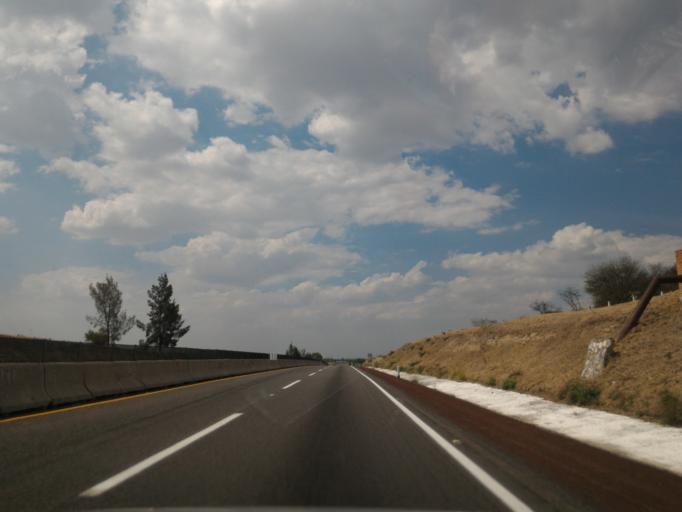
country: MX
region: Jalisco
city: Encarnacion de Diaz
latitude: 21.5713
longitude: -102.2744
